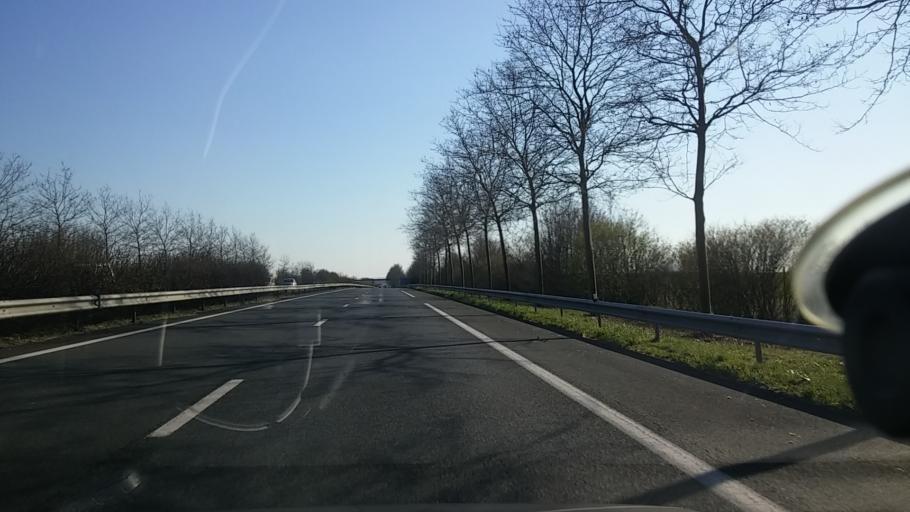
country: FR
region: Centre
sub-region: Departement de l'Indre
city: Montierchaume
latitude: 46.9087
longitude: 1.7366
